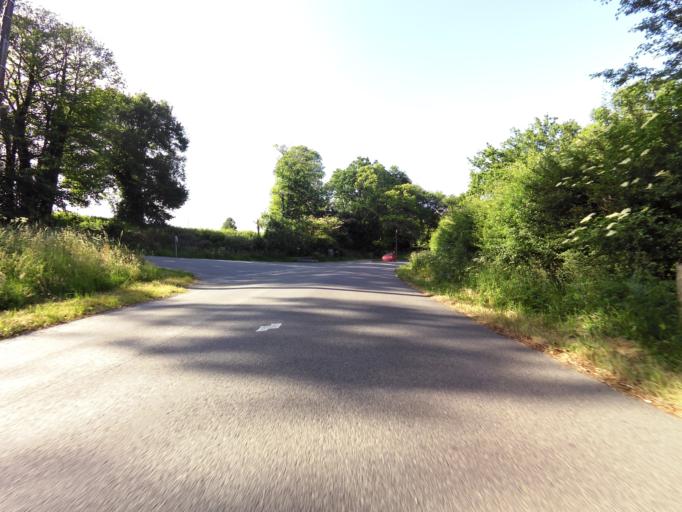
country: FR
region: Brittany
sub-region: Departement du Morbihan
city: Pluherlin
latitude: 47.6963
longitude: -2.3461
